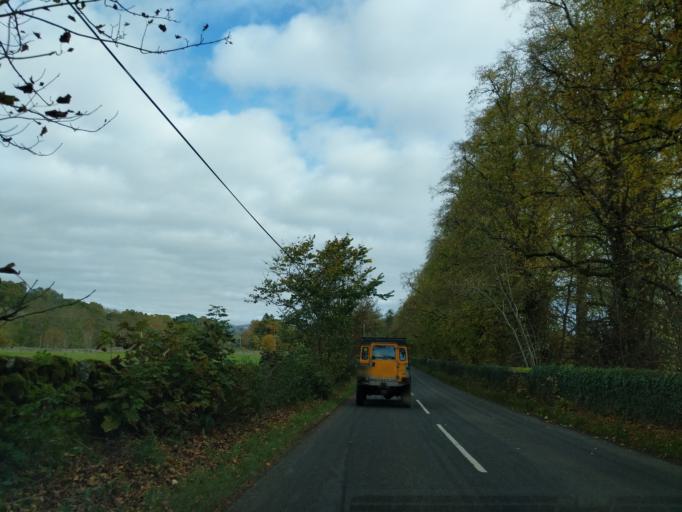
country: GB
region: Scotland
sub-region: Dumfries and Galloway
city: Thornhill
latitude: 55.2284
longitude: -3.8296
